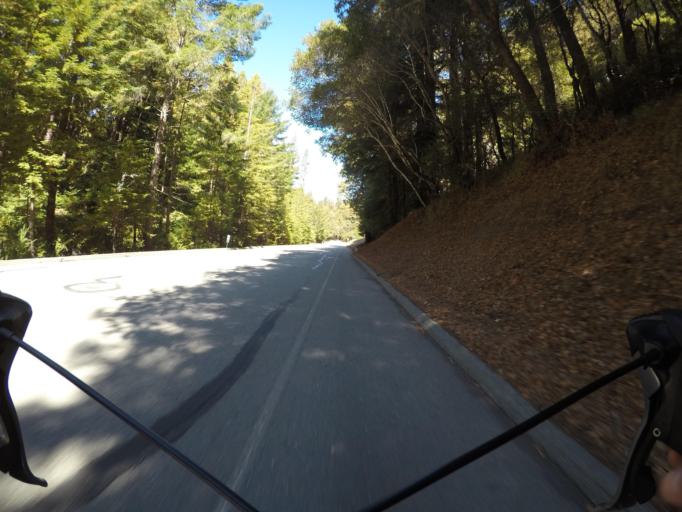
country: US
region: California
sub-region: San Mateo County
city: Portola Valley
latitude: 37.3048
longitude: -122.2682
